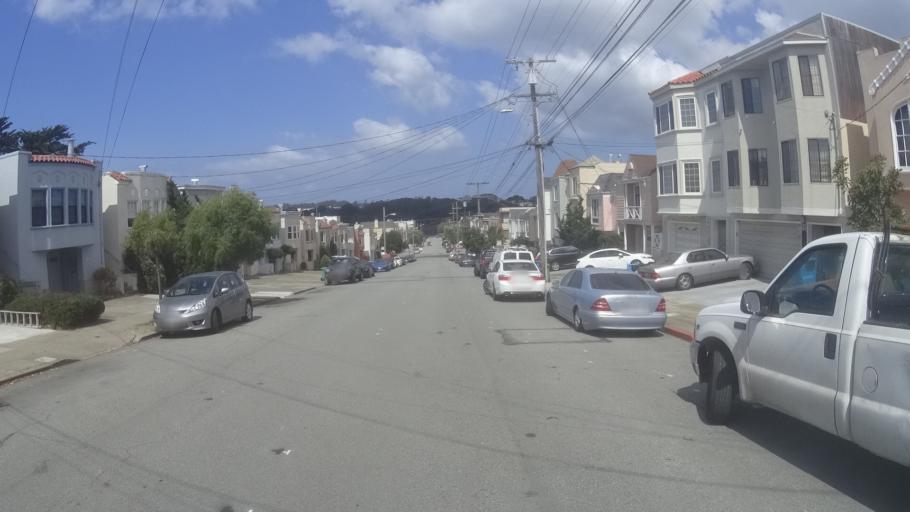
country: US
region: California
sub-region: San Mateo County
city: Daly City
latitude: 37.7615
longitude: -122.4931
